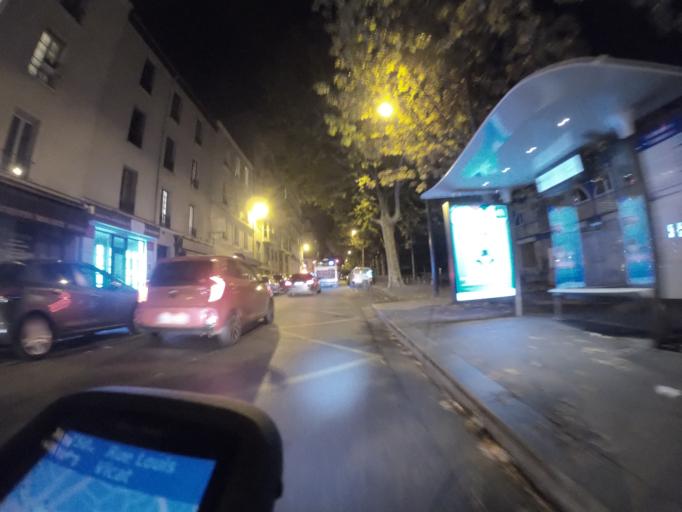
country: FR
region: Ile-de-France
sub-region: Departement des Hauts-de-Seine
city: Malakoff
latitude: 48.8320
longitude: 2.3028
